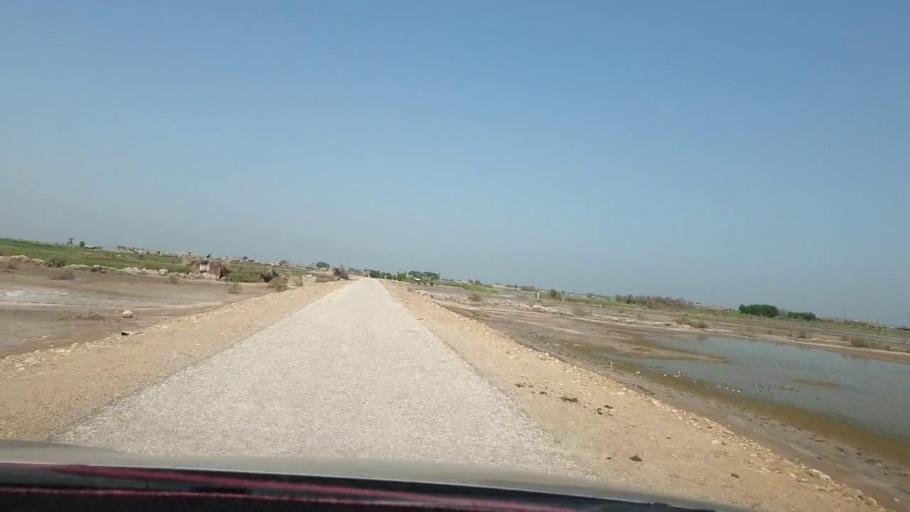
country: PK
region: Sindh
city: Warah
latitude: 27.5709
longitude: 67.7555
